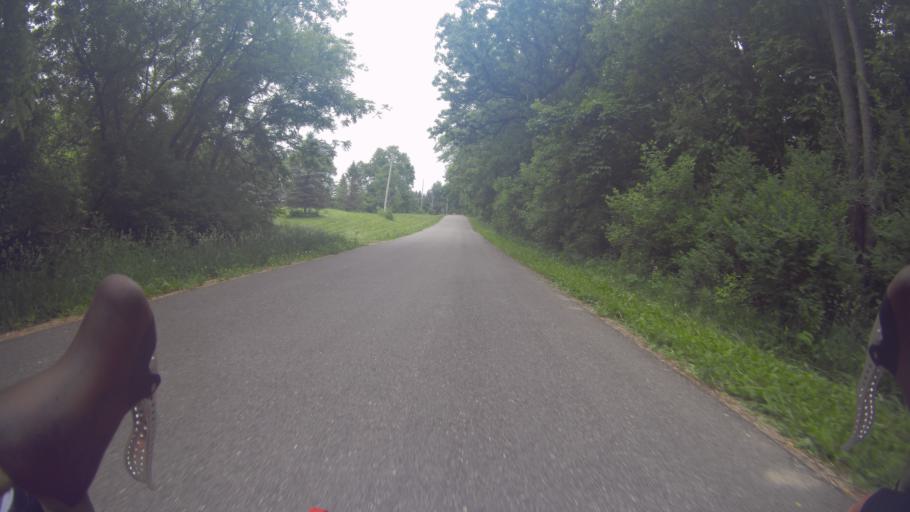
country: US
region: Wisconsin
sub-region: Green County
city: Brooklyn
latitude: 42.8690
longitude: -89.3596
